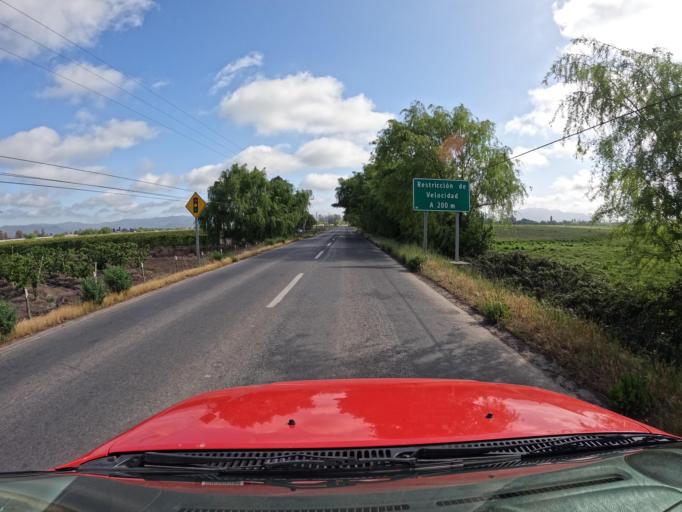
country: CL
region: Maule
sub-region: Provincia de Curico
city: Rauco
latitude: -34.8937
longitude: -71.2739
